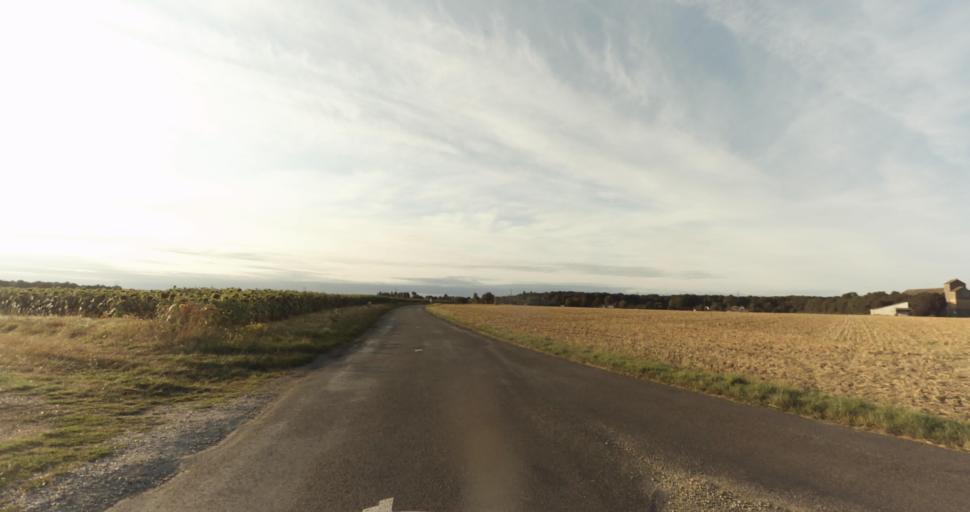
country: FR
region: Haute-Normandie
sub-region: Departement de l'Eure
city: Marcilly-sur-Eure
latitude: 48.8393
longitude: 1.2802
